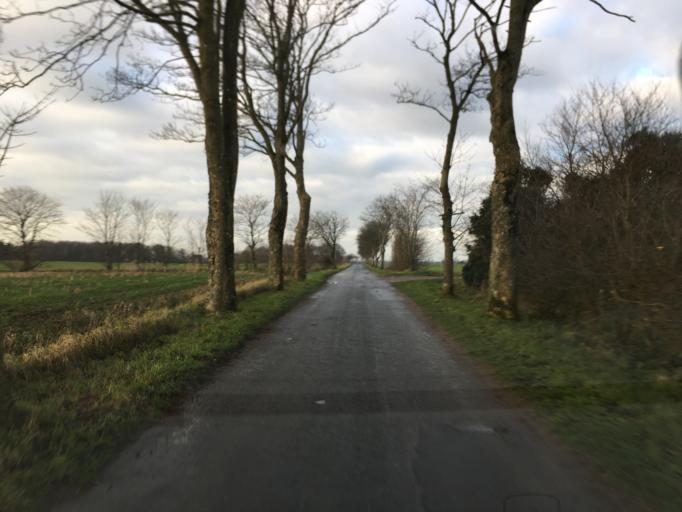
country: DK
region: South Denmark
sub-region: Tonder Kommune
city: Logumkloster
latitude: 55.1145
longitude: 8.8754
